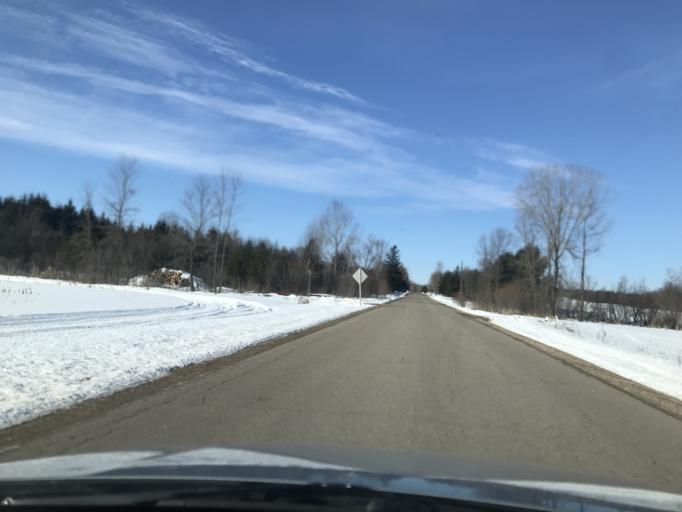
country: US
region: Wisconsin
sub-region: Oconto County
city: Oconto Falls
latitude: 44.9232
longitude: -88.1694
